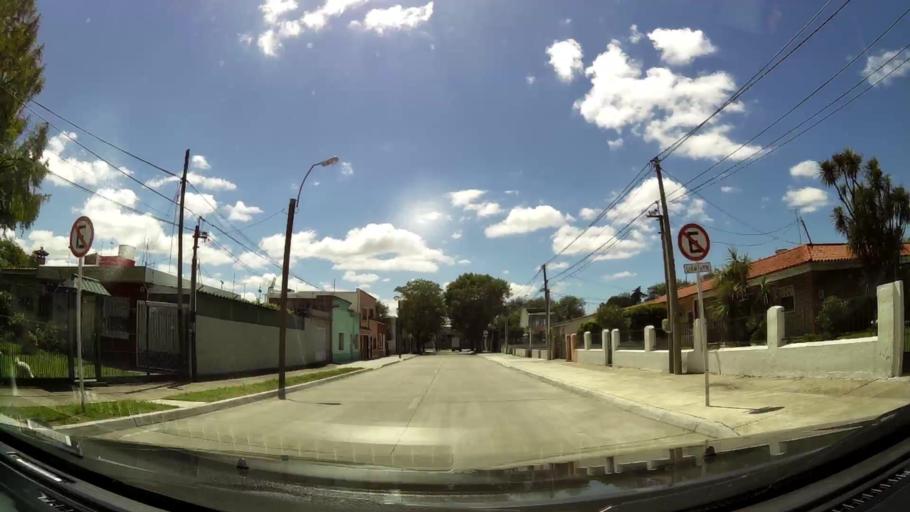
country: UY
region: Montevideo
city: Montevideo
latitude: -34.8532
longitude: -56.1323
